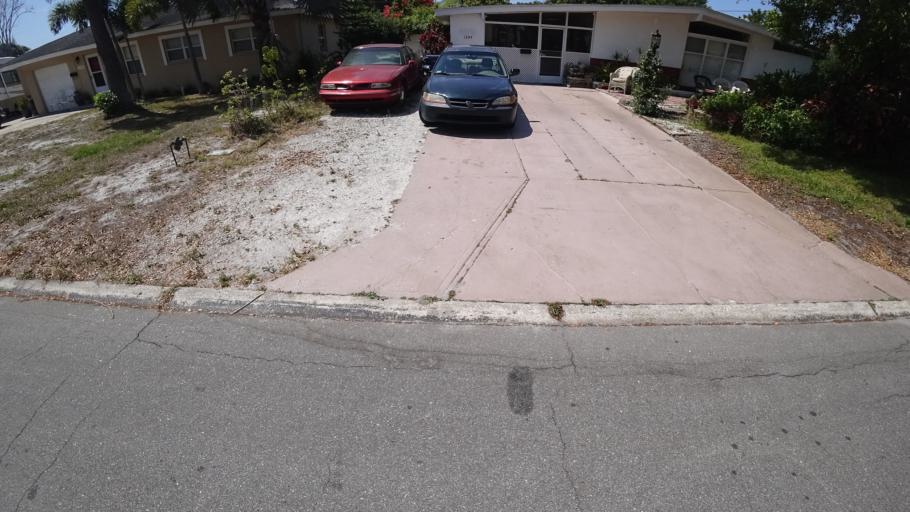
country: US
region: Florida
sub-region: Manatee County
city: Bayshore Gardens
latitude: 27.4284
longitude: -82.5809
